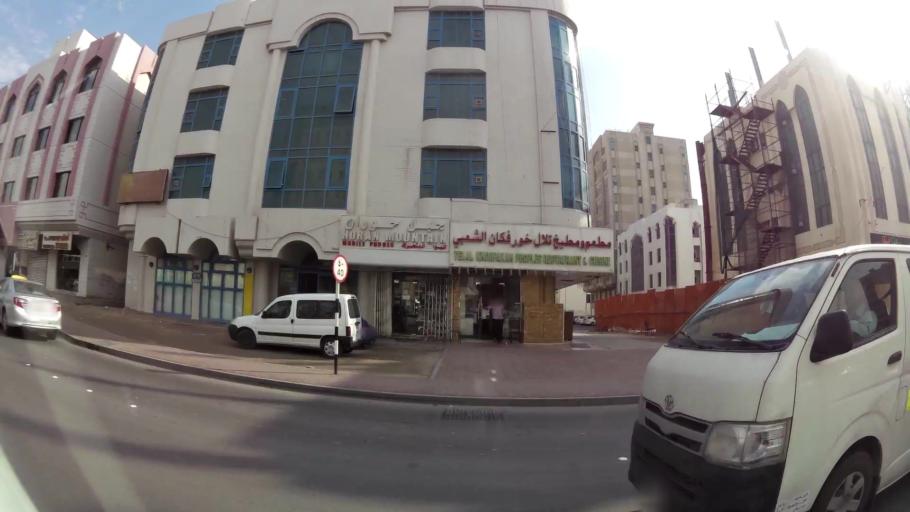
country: AE
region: Abu Dhabi
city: Abu Dhabi
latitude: 24.3246
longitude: 54.5359
